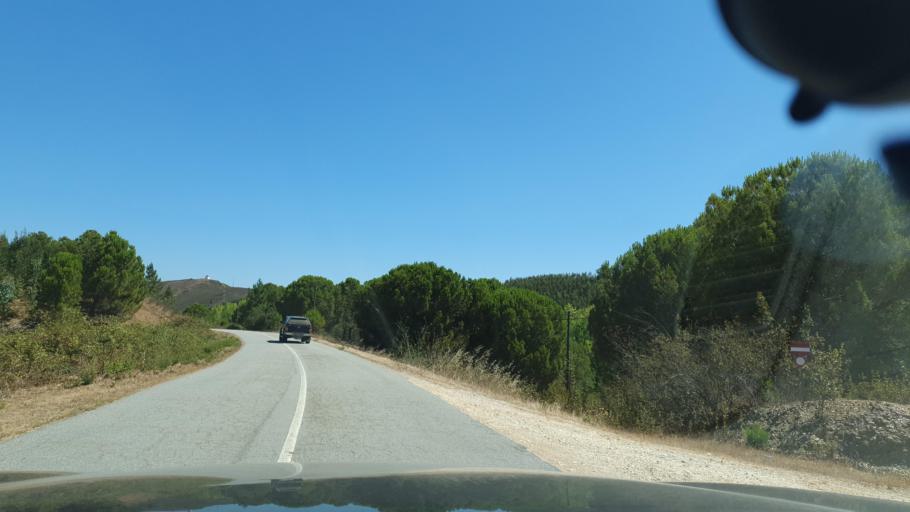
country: PT
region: Faro
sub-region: Monchique
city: Monchique
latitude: 37.4260
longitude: -8.5331
